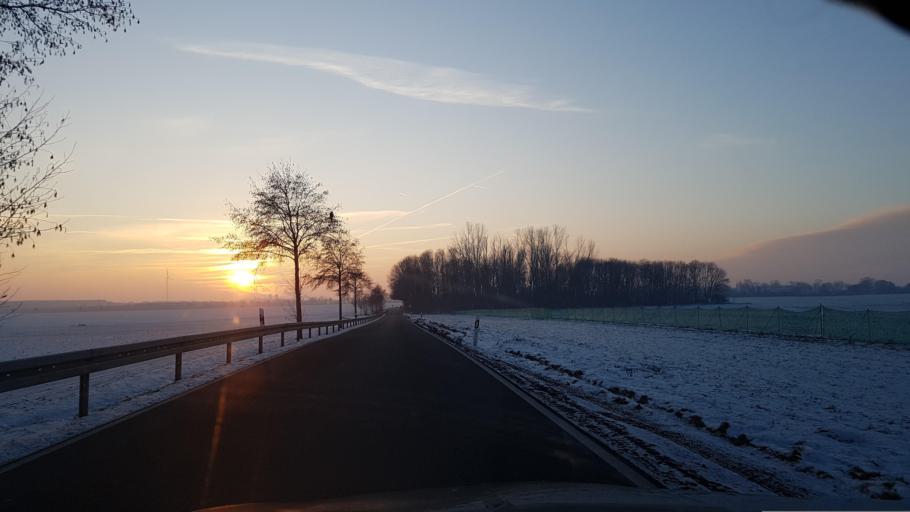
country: DE
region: Saxony
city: Krostitz
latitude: 51.4221
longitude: 12.4664
